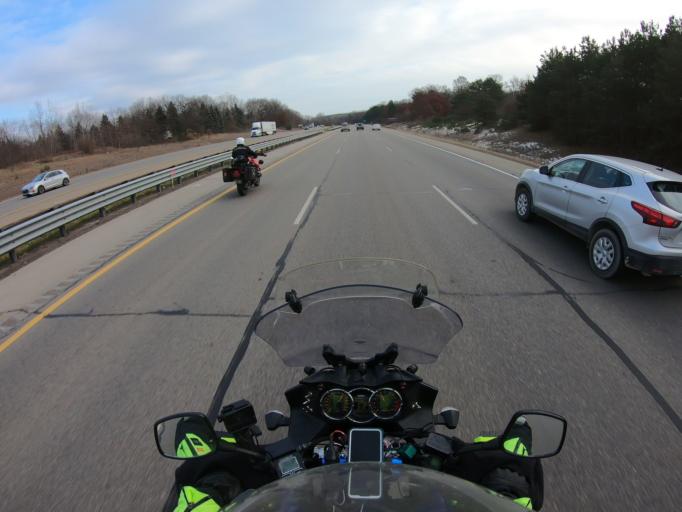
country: US
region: Michigan
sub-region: Oakland County
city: Clarkston
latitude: 42.7423
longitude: -83.4751
